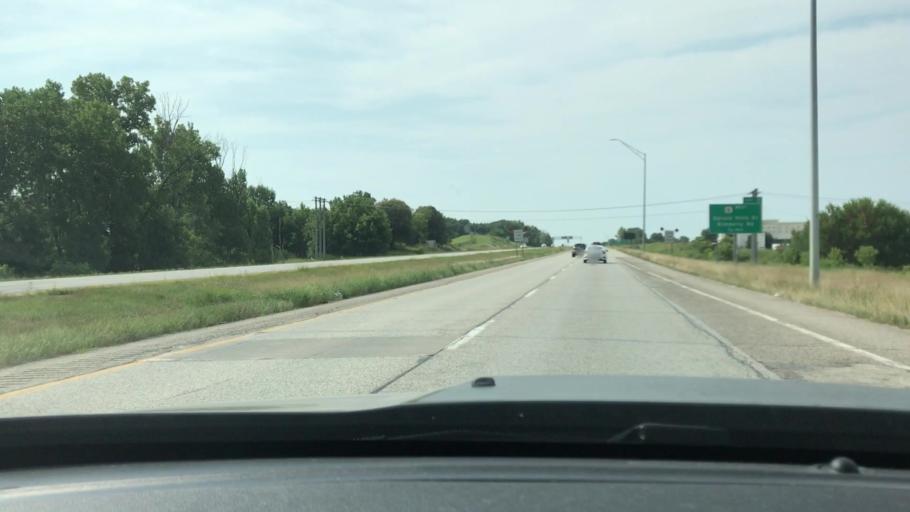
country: US
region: Iowa
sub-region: Scott County
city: Bettendorf
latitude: 41.5693
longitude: -90.5225
